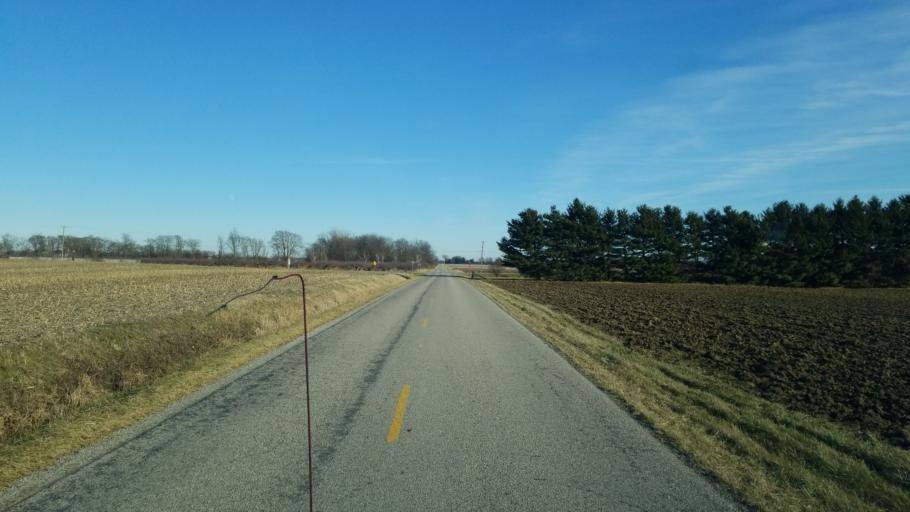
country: US
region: Ohio
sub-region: Sandusky County
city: Mount Carmel
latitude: 41.2561
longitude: -82.9774
